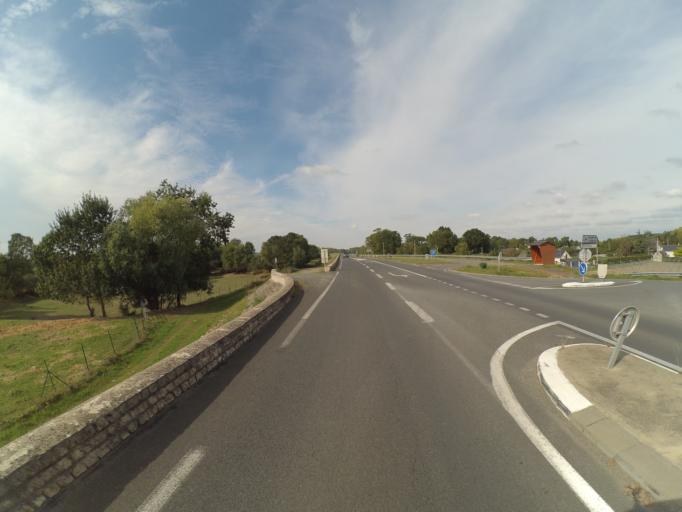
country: FR
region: Pays de la Loire
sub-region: Departement de Maine-et-Loire
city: Villebernier
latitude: 47.2450
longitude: 0.0023
